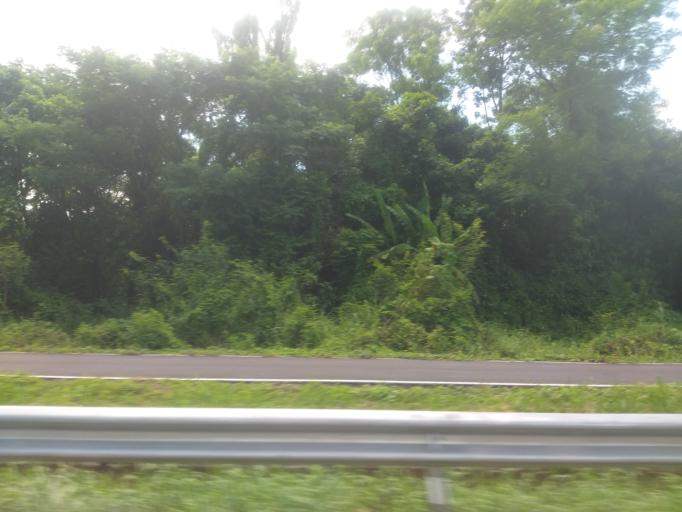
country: TH
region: Nakhon Nayok
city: Nakhon Nayok
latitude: 14.2974
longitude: 101.3059
